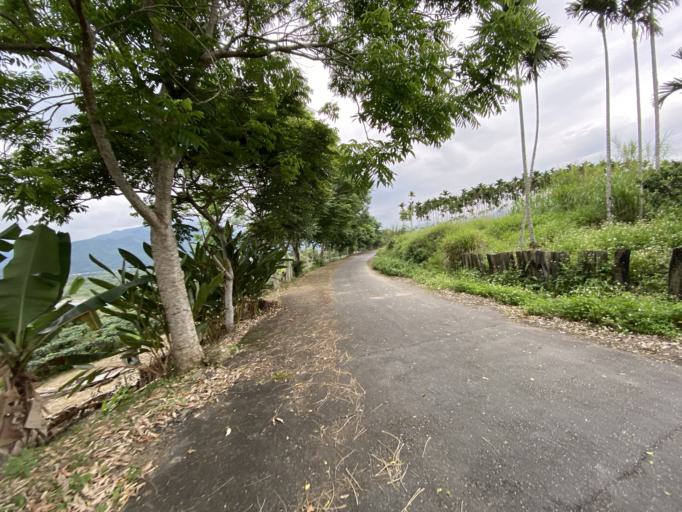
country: TW
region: Taiwan
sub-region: Hualien
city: Hualian
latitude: 23.4710
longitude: 121.3590
